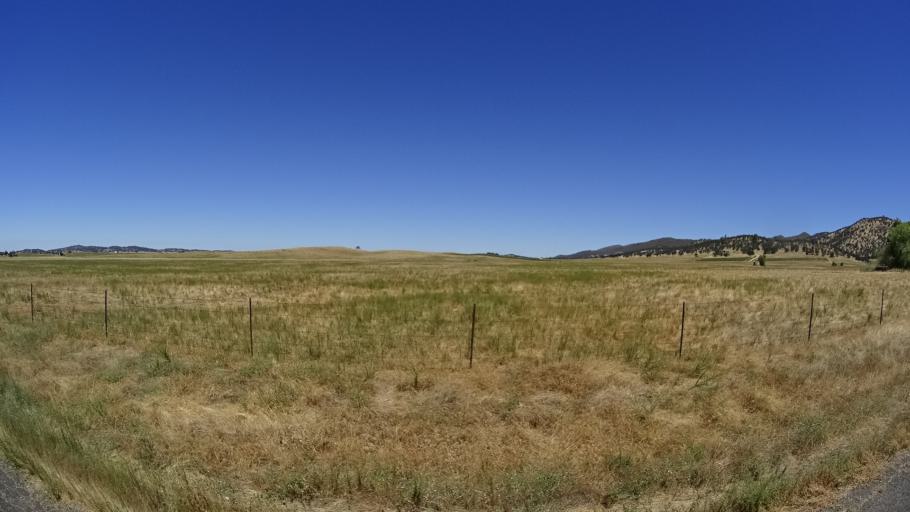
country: US
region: California
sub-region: Calaveras County
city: Copperopolis
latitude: 38.0383
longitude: -120.7022
